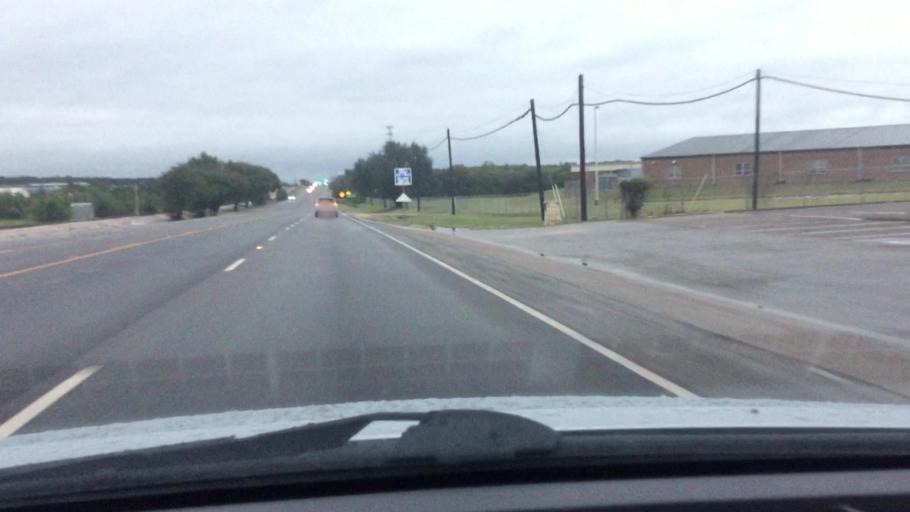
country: US
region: Texas
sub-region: Williamson County
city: Leander
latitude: 30.5751
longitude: -97.8514
